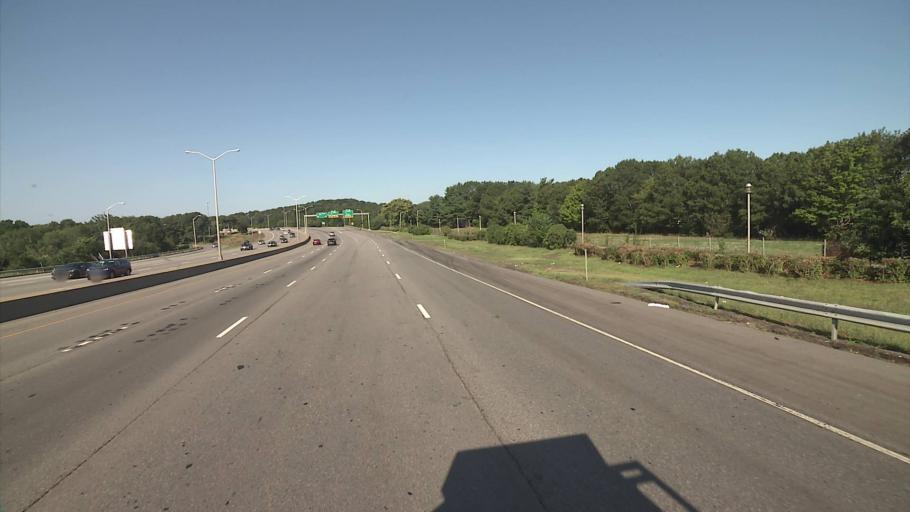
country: US
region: Connecticut
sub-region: Middlesex County
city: Old Saybrook Center
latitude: 41.3182
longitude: -72.3534
